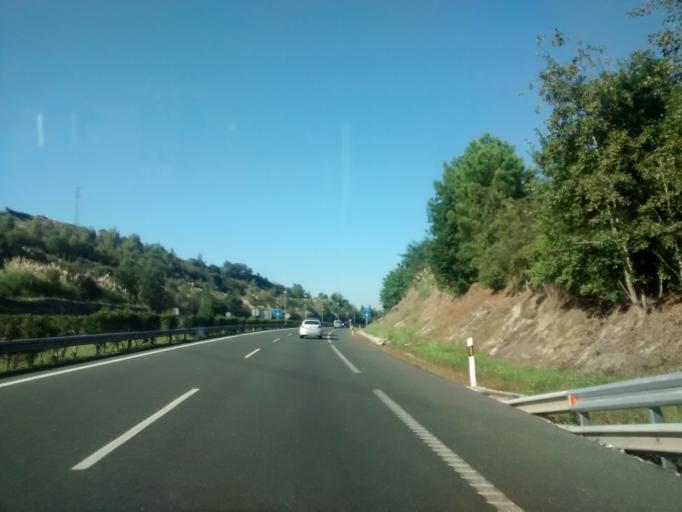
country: ES
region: Cantabria
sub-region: Provincia de Cantabria
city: Reocin
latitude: 43.3540
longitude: -4.0824
